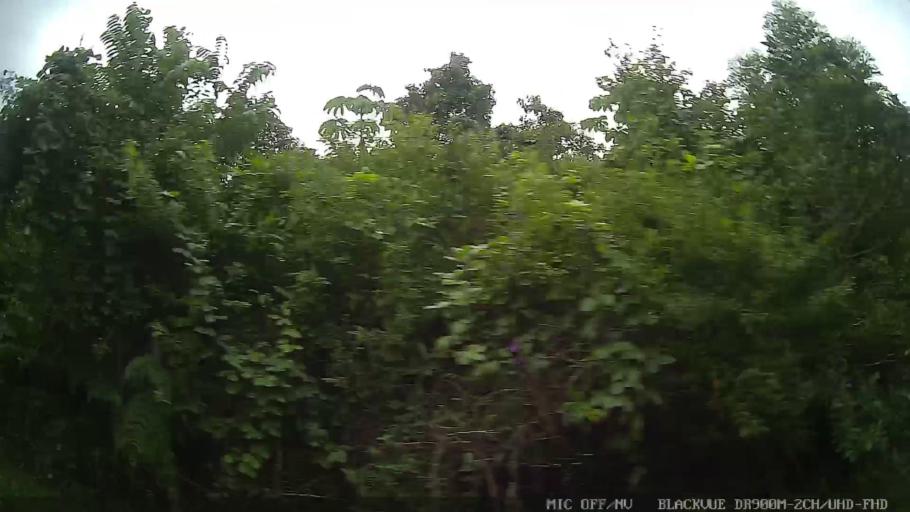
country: BR
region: Sao Paulo
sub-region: Iguape
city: Iguape
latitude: -24.6862
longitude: -47.4805
